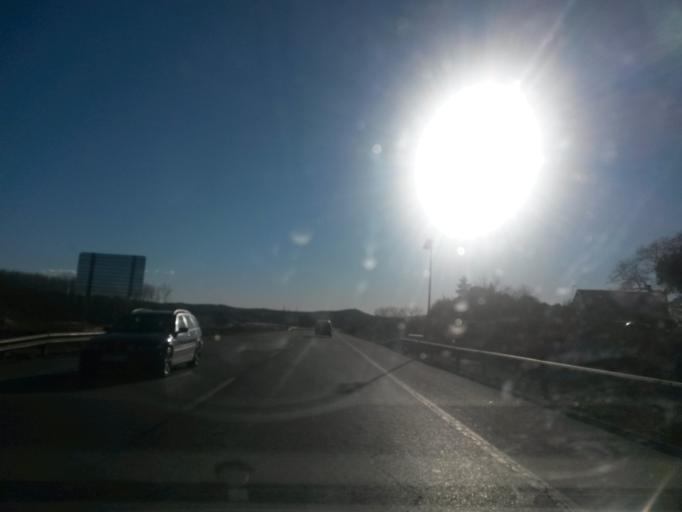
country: ES
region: Catalonia
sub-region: Provincia de Girona
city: Sils
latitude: 41.7977
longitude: 2.7601
